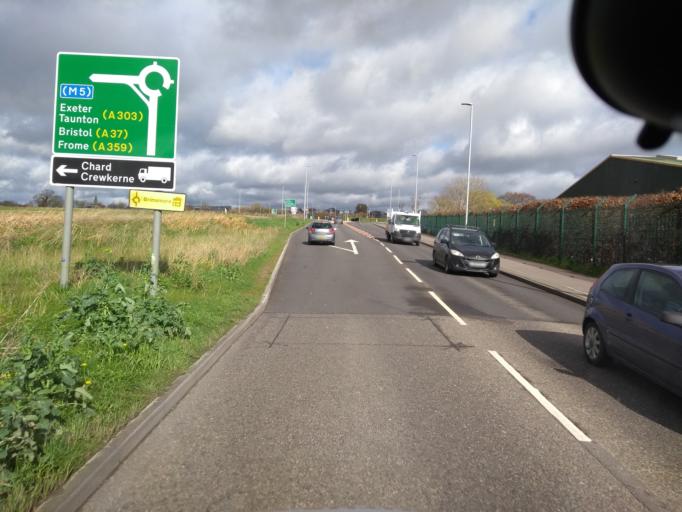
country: GB
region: England
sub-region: Somerset
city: Yeovil
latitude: 50.9371
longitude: -2.6688
